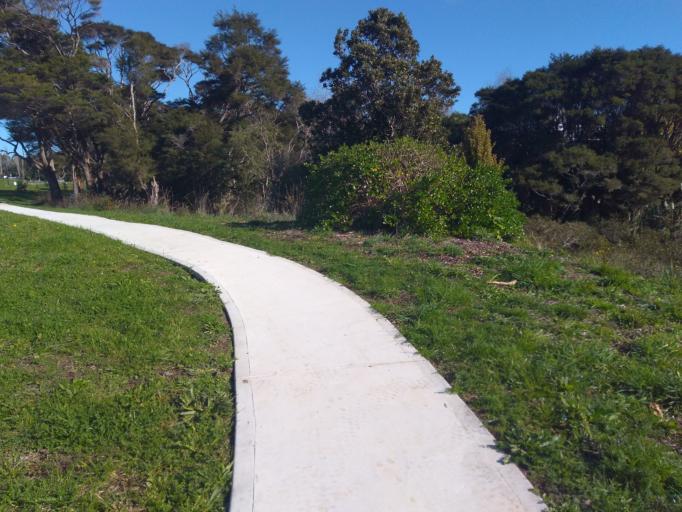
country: NZ
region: Auckland
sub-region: Auckland
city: Pakuranga
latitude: -36.9461
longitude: 174.9668
